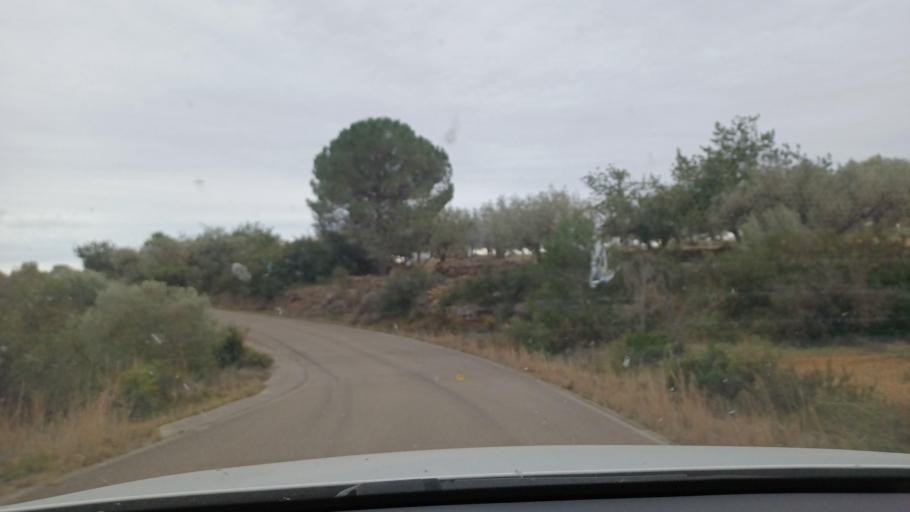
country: ES
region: Valencia
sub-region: Provincia de Castello
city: Canet lo Roig
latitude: 40.5958
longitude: 0.2824
